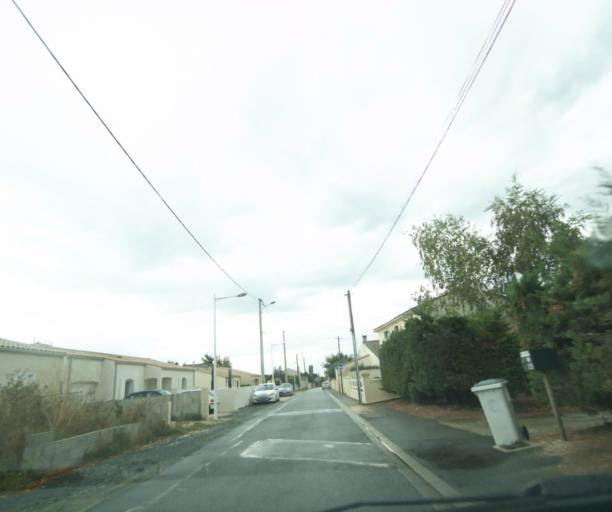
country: FR
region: Poitou-Charentes
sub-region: Departement de la Charente-Maritime
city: Tonnay-Charente
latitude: 45.9515
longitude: -0.8782
